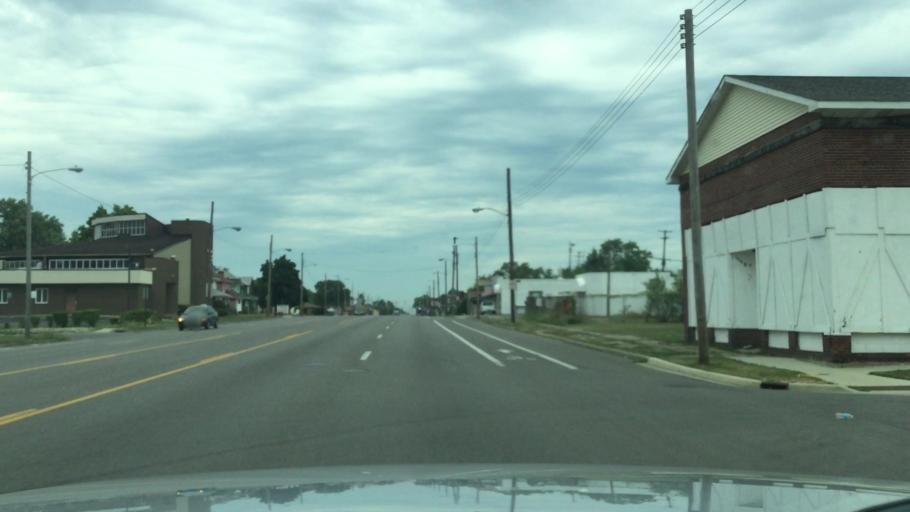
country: US
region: Michigan
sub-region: Genesee County
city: Beecher
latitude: 43.0575
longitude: -83.6938
